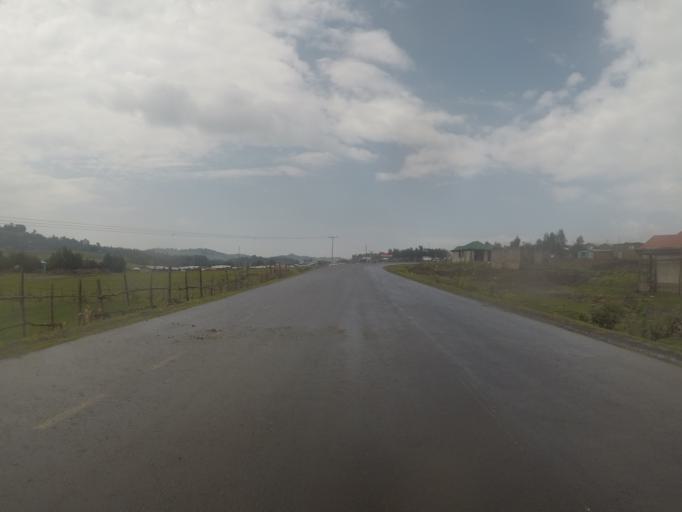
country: ET
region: Amhara
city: Debark'
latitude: 13.1339
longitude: 37.8916
